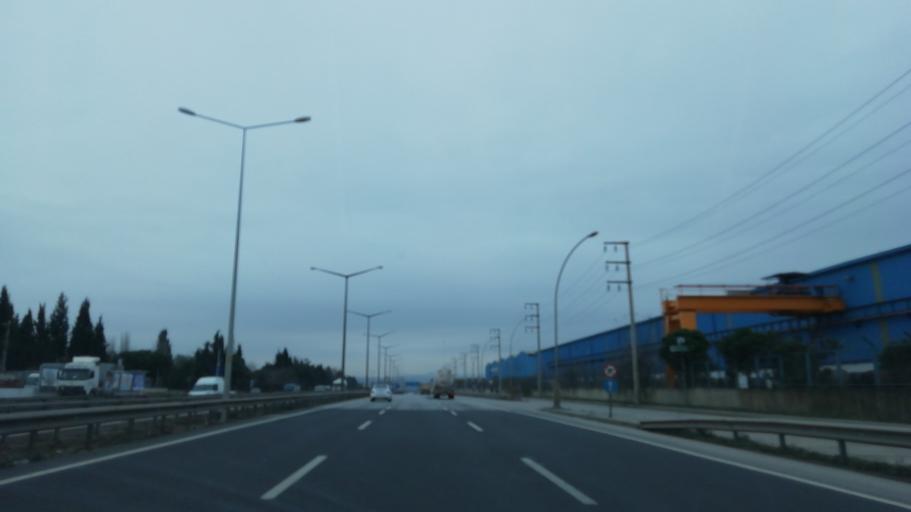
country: TR
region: Kocaeli
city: Gebze
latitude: 40.7989
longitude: 29.4494
